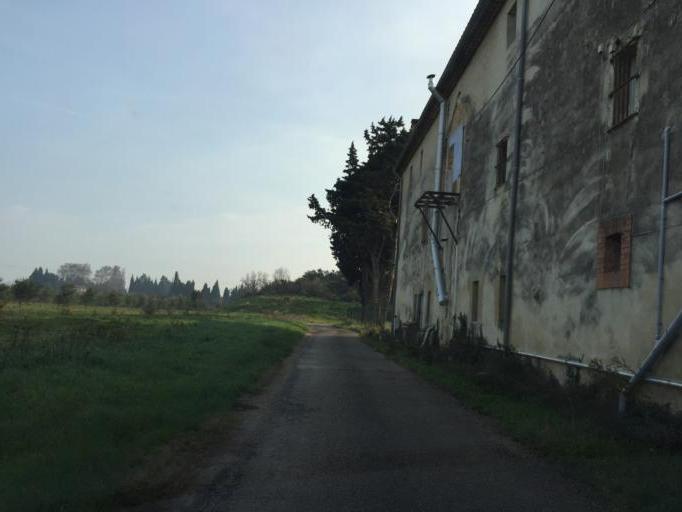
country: FR
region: Provence-Alpes-Cote d'Azur
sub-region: Departement du Vaucluse
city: Orange
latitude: 44.1347
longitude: 4.8358
